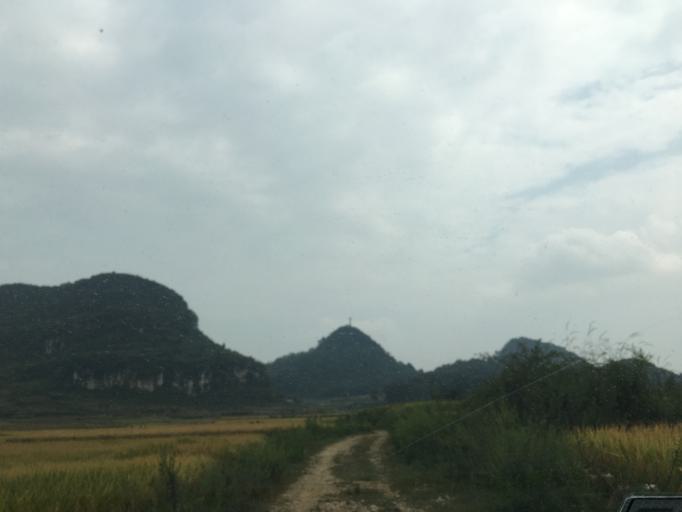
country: CN
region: Guangxi Zhuangzu Zizhiqu
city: Xinzhou
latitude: 25.4936
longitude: 105.6516
